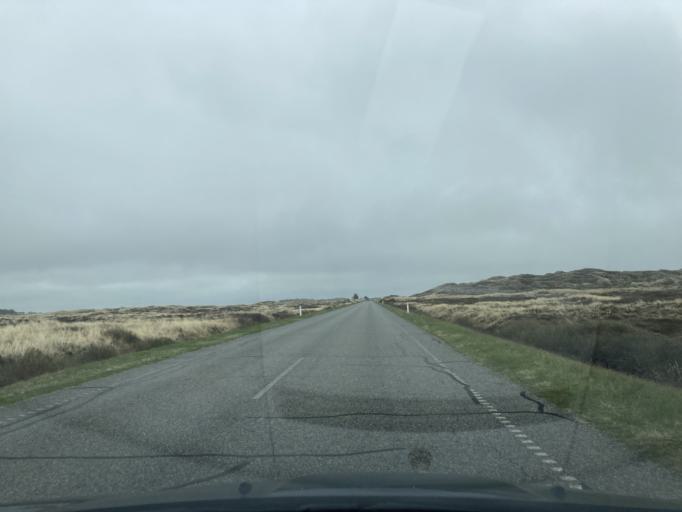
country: DK
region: North Denmark
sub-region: Thisted Kommune
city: Hurup
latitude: 56.9281
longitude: 8.3459
